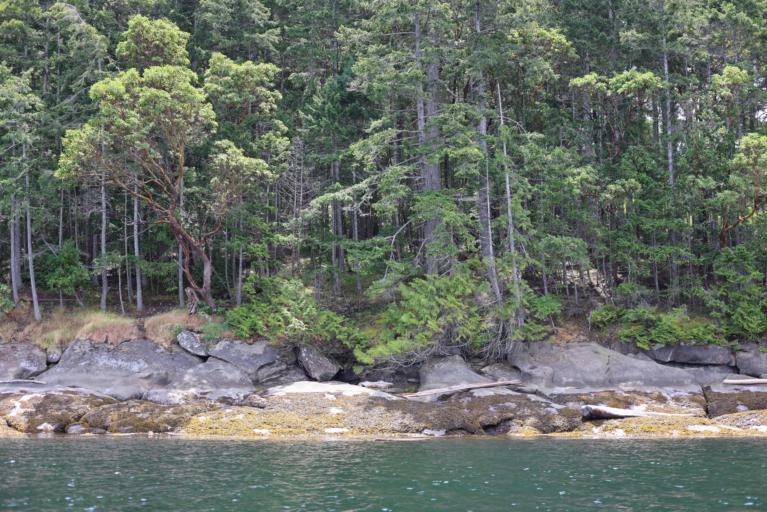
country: CA
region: British Columbia
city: Nanaimo
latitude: 49.1364
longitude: -123.8233
